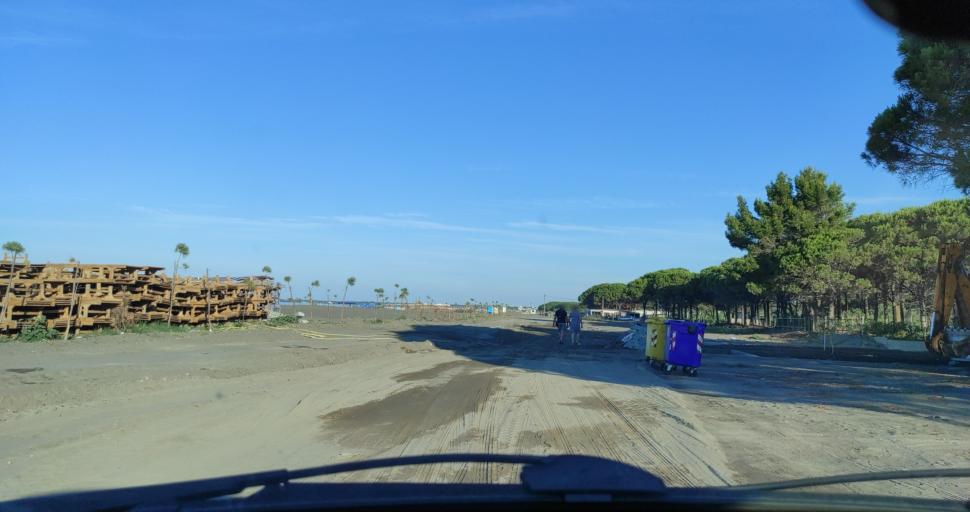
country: AL
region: Shkoder
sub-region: Rrethi i Shkodres
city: Velipoje
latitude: 41.8596
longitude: 19.4420
